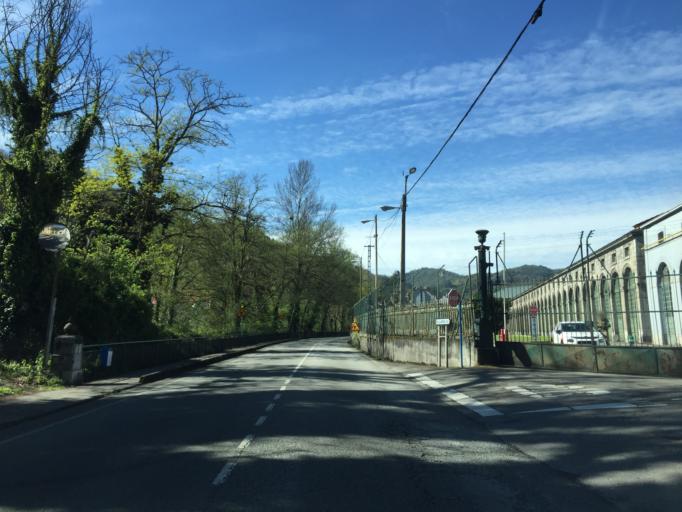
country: ES
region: Asturias
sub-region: Province of Asturias
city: Castandiello
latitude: 43.3471
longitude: -5.9708
